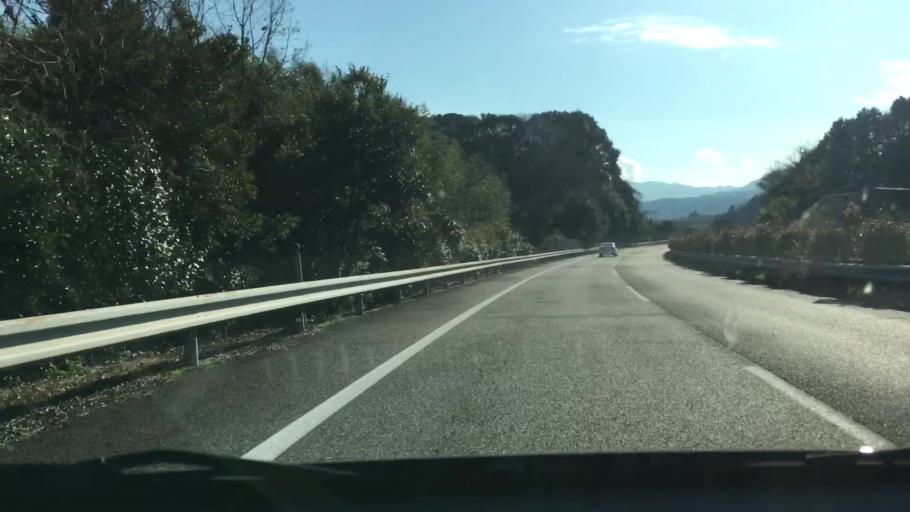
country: JP
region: Kumamoto
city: Hitoyoshi
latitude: 32.2174
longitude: 130.7799
